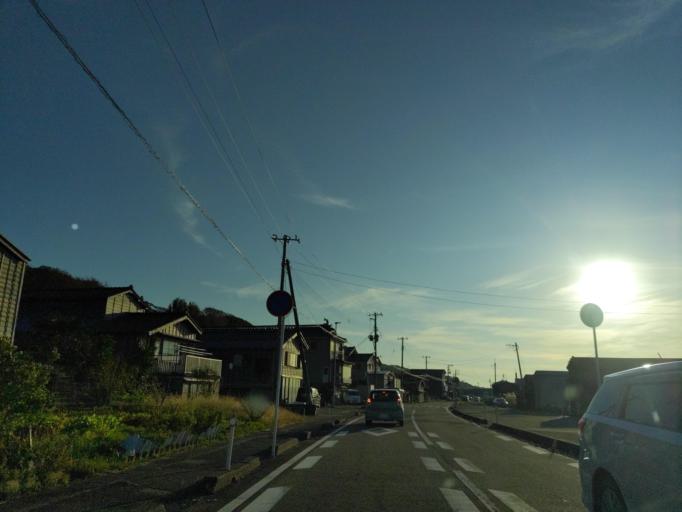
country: JP
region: Niigata
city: Nagaoka
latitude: 37.5419
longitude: 138.6854
